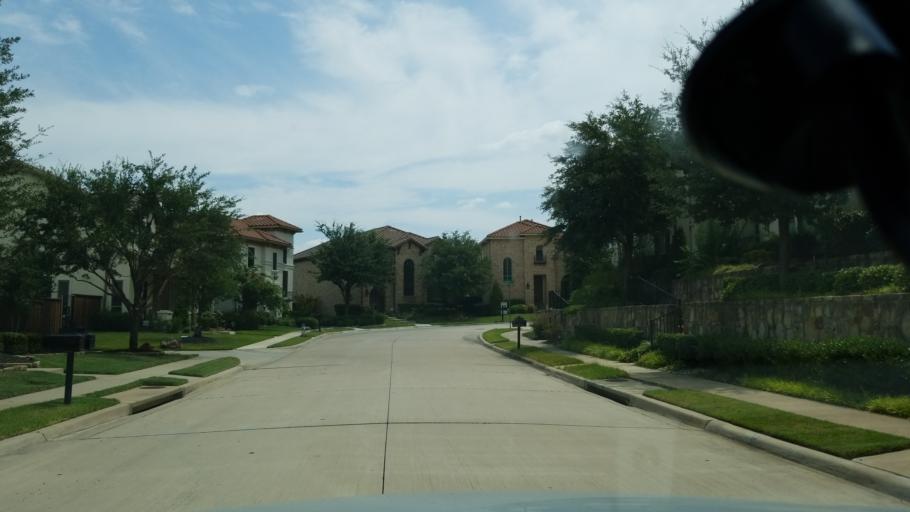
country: US
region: Texas
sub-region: Dallas County
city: Farmers Branch
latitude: 32.9037
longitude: -96.9426
